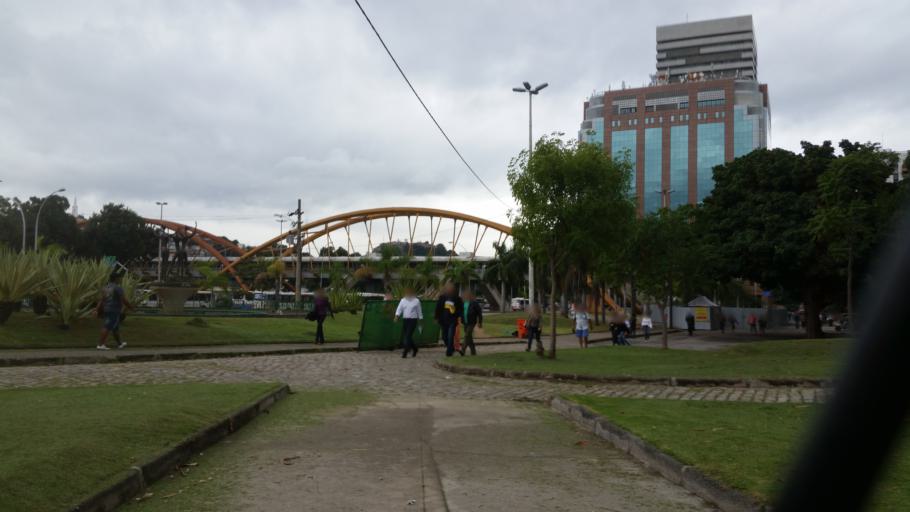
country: BR
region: Rio de Janeiro
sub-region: Rio De Janeiro
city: Rio de Janeiro
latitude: -22.9112
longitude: -43.2066
